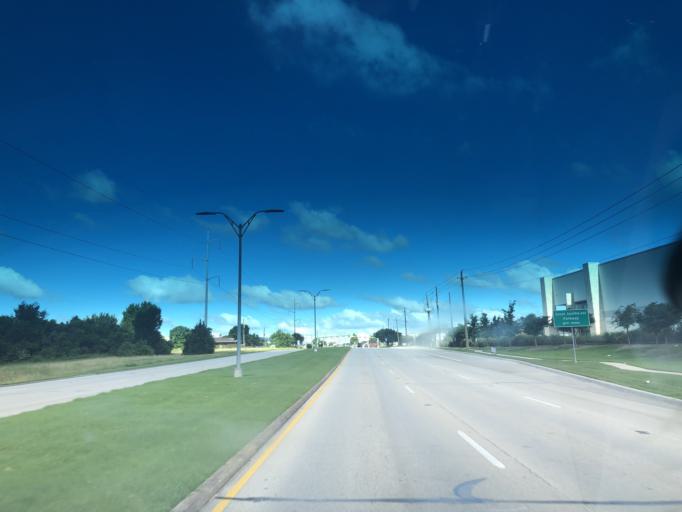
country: US
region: Texas
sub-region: Dallas County
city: Grand Prairie
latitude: 32.7115
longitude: -97.0400
